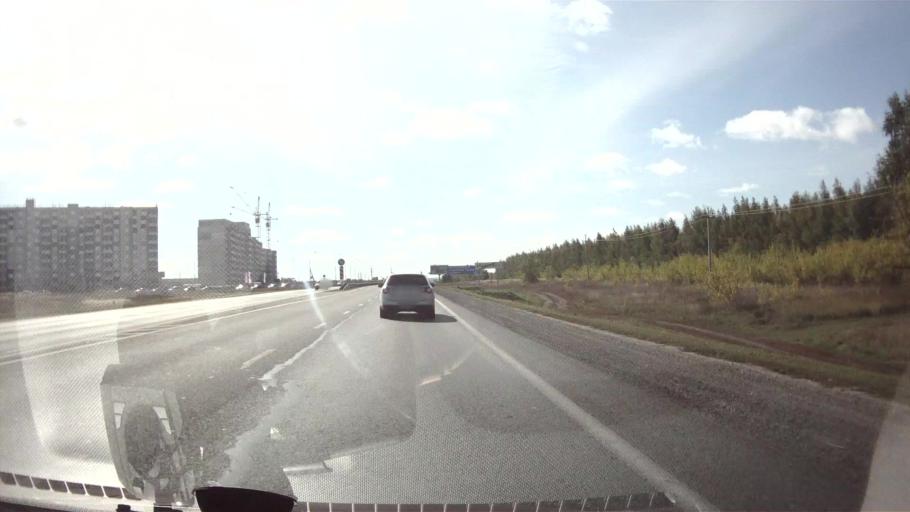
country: RU
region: Ulyanovsk
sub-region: Ulyanovskiy Rayon
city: Ulyanovsk
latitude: 54.2850
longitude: 48.2571
